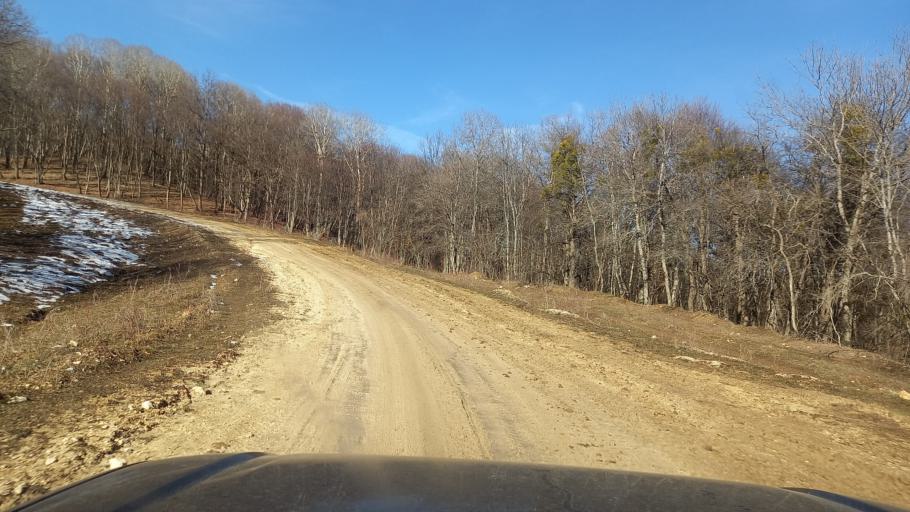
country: RU
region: Adygeya
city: Kamennomostskiy
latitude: 44.2823
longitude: 40.3207
